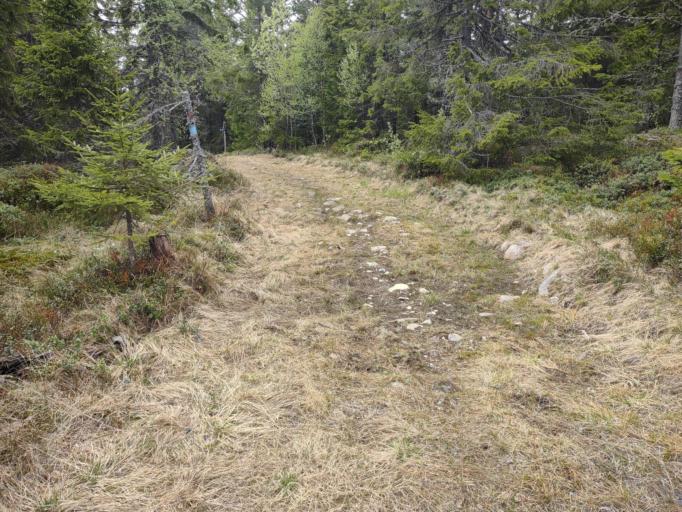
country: NO
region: Oppland
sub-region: Gran
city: Jaren
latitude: 60.4640
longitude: 10.5836
